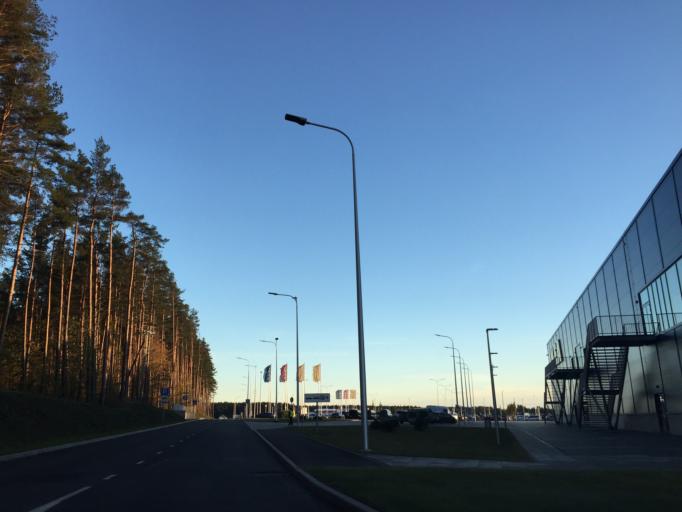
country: LV
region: Stopini
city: Ulbroka
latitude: 56.9553
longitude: 24.2568
